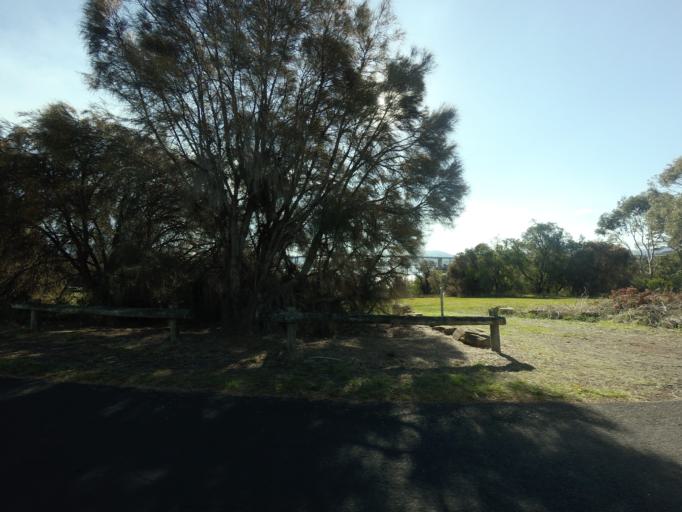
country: AU
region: Tasmania
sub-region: Clarence
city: Bellerive
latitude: -42.8706
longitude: 147.3533
